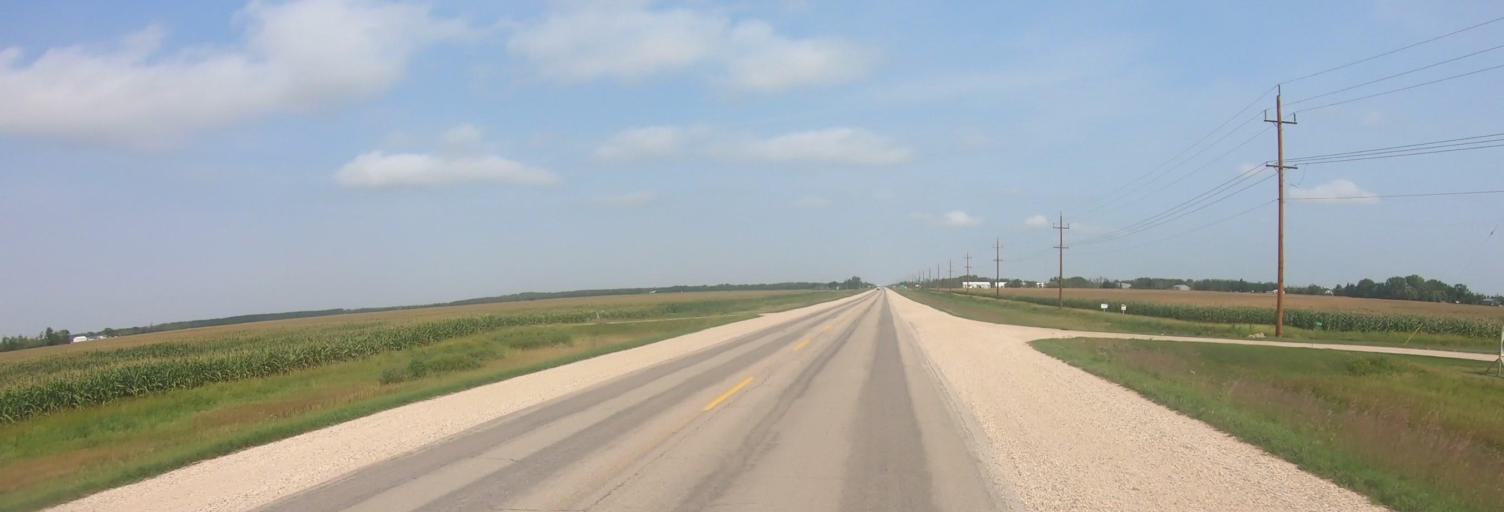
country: CA
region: Manitoba
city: Steinbach
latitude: 49.4674
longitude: -96.6911
